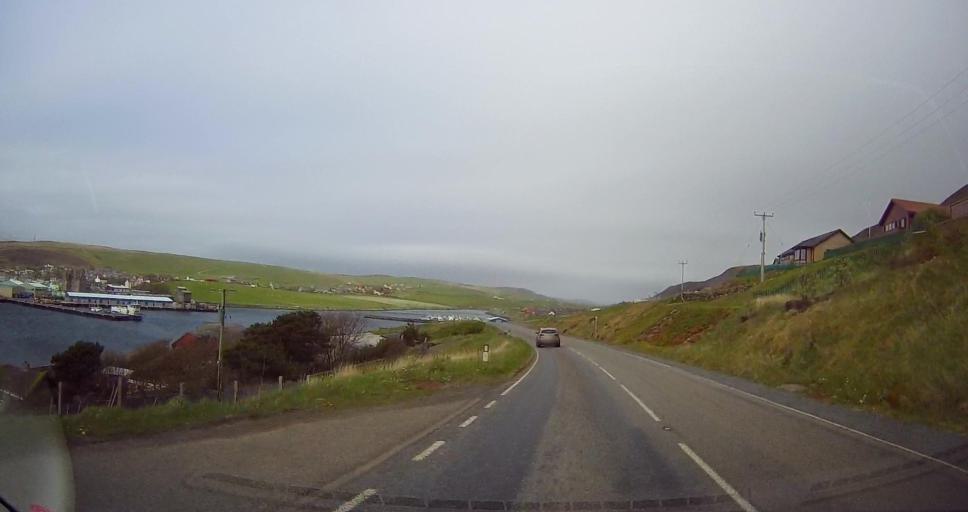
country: GB
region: Scotland
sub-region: Shetland Islands
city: Lerwick
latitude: 60.1314
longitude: -1.2676
